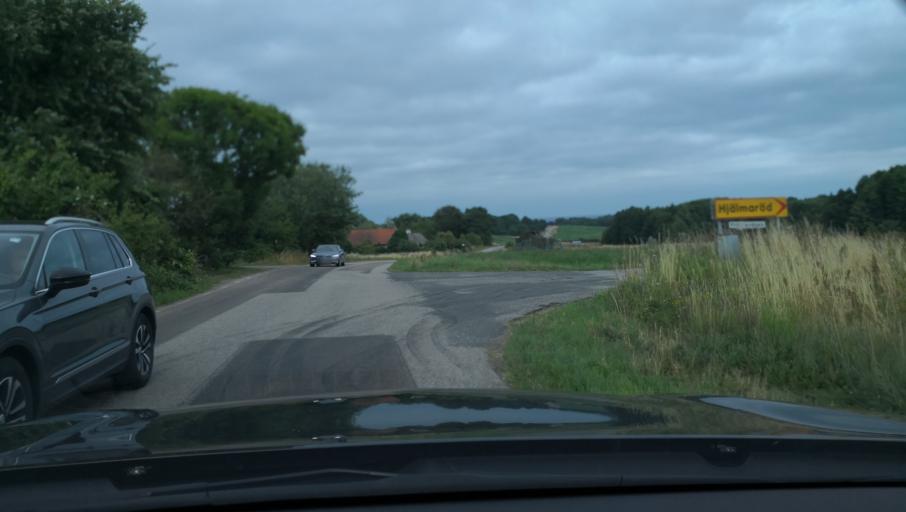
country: SE
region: Skane
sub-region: Simrishamns Kommun
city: Kivik
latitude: 55.6962
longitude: 14.1735
